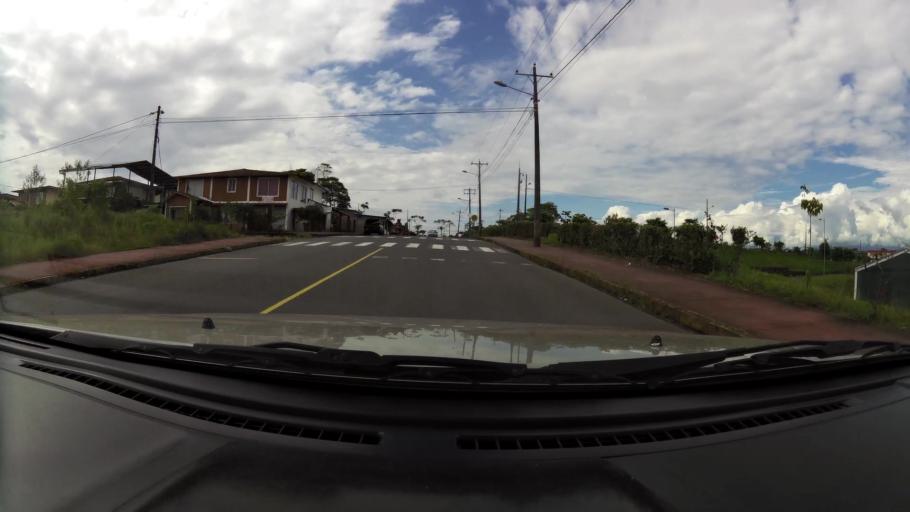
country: EC
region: Pastaza
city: Puyo
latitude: -1.5024
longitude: -78.0022
